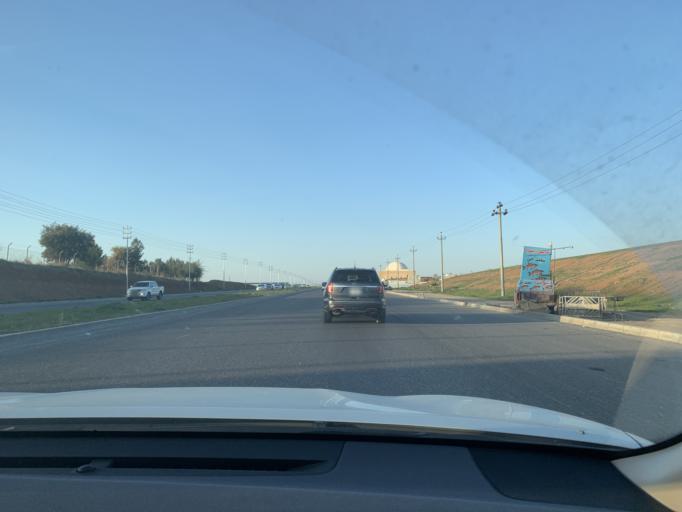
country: IQ
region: Arbil
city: Erbil
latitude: 36.2761
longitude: 44.0154
